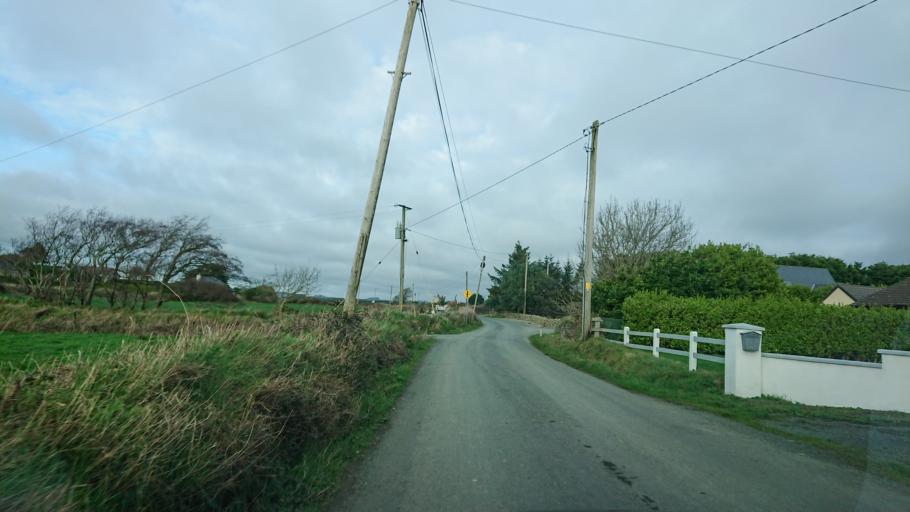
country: IE
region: Munster
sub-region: Waterford
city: Portlaw
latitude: 52.1495
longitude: -7.3091
